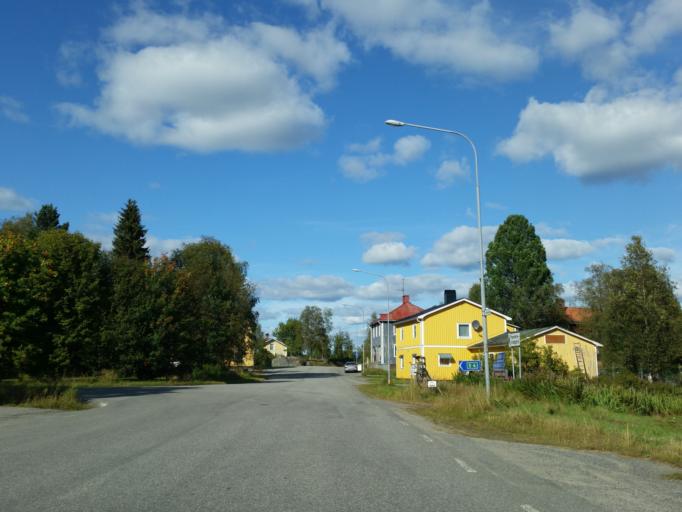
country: SE
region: Vaesterbotten
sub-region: Robertsfors Kommun
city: Robertsfors
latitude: 64.0587
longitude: 20.8544
